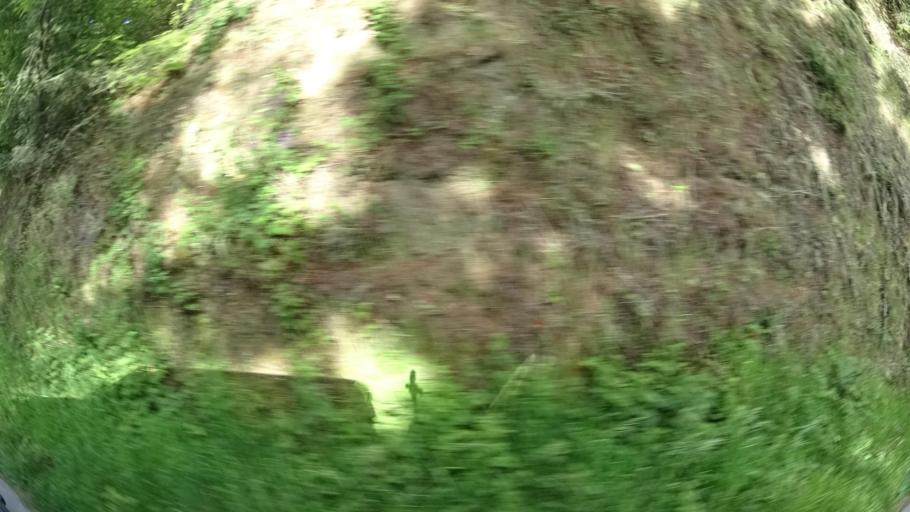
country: US
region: California
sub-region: Humboldt County
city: Ferndale
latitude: 40.5594
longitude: -124.2727
